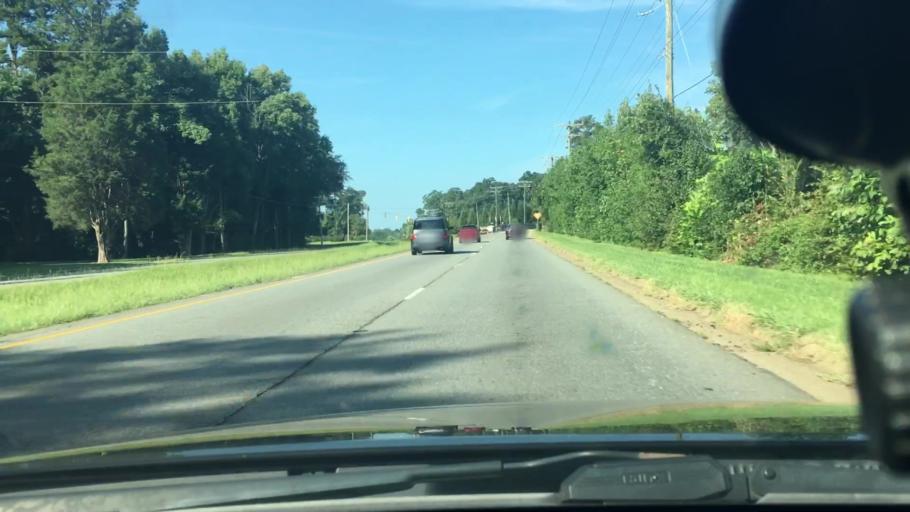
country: US
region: North Carolina
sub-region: Mecklenburg County
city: Mint Hill
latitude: 35.2178
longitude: -80.6542
